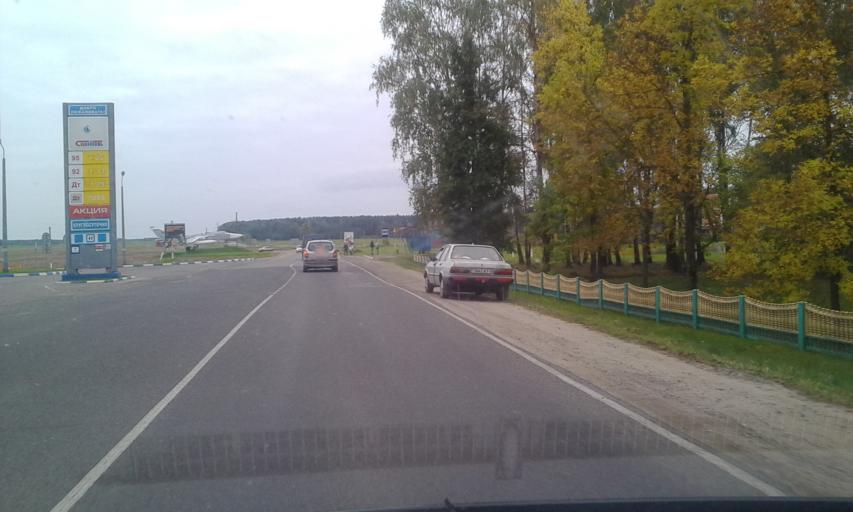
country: BY
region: Vitebsk
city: Pastavy
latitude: 55.1116
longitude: 26.8729
